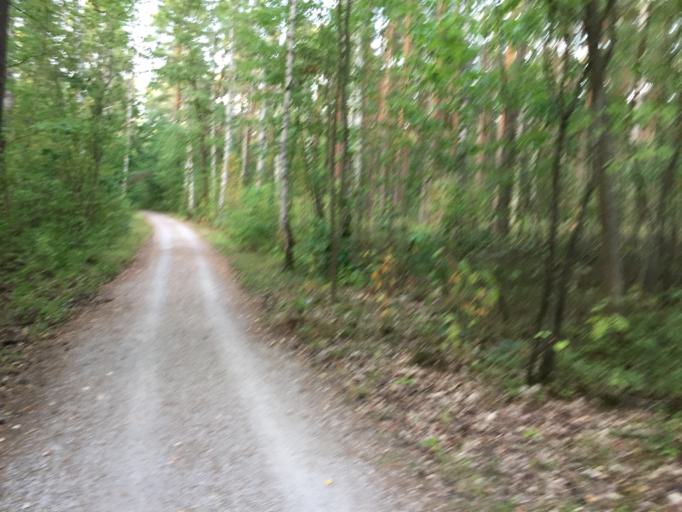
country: DE
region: Bavaria
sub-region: Regierungsbezirk Mittelfranken
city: Erlangen
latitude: 49.5706
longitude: 11.0168
